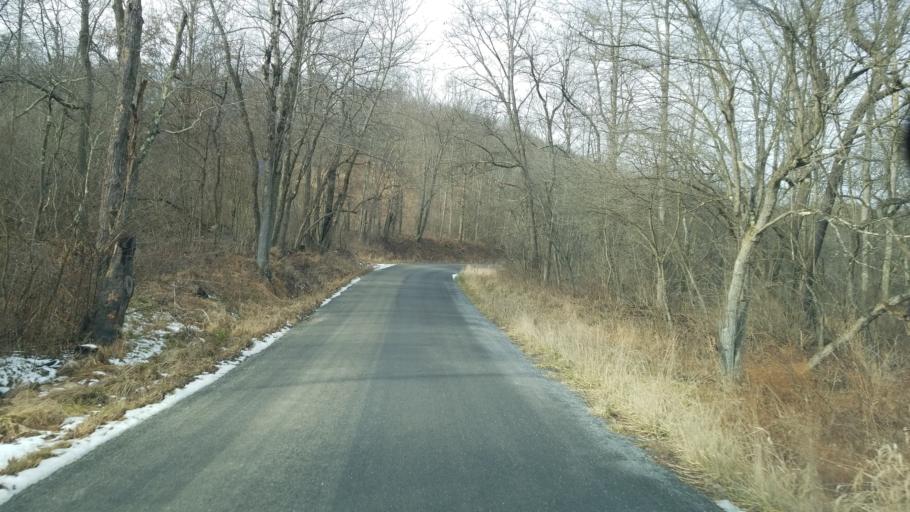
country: US
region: Pennsylvania
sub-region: Jefferson County
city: Punxsutawney
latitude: 40.8706
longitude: -79.0512
